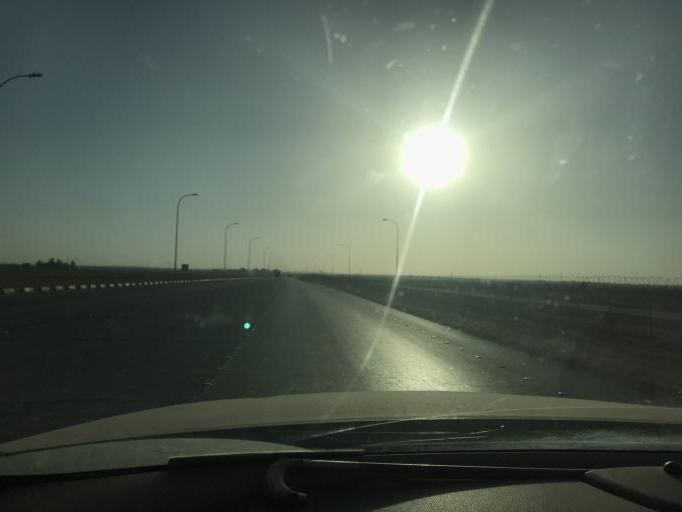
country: SA
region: Ar Riyad
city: Riyadh
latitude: 24.9243
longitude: 46.7129
